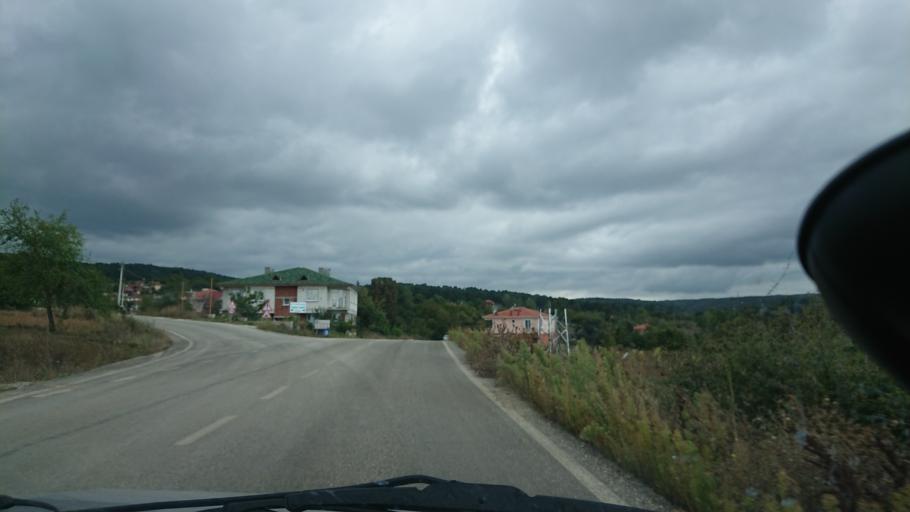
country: TR
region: Bilecik
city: Pazaryeri
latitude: 40.0098
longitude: 29.8057
